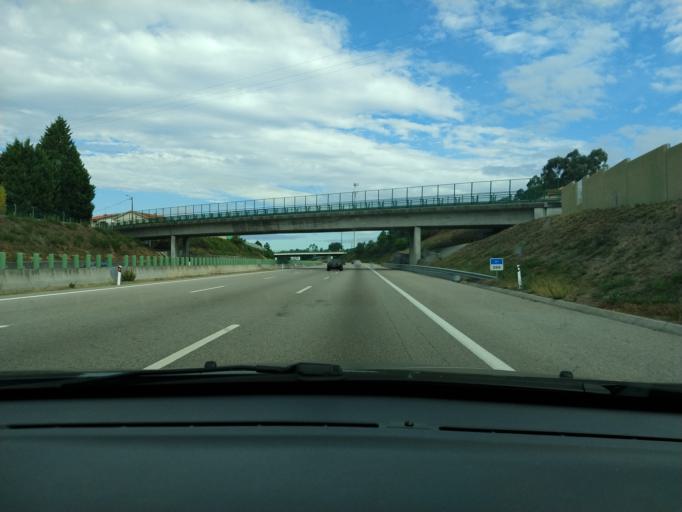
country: PT
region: Aveiro
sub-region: Ovar
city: Valega
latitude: 40.8778
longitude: -8.5604
